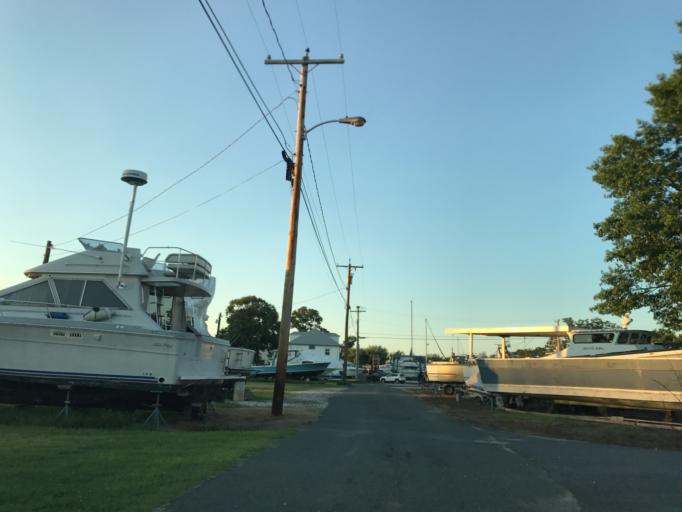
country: US
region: Maryland
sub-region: Baltimore County
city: Bowleys Quarters
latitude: 39.3304
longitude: -76.4047
